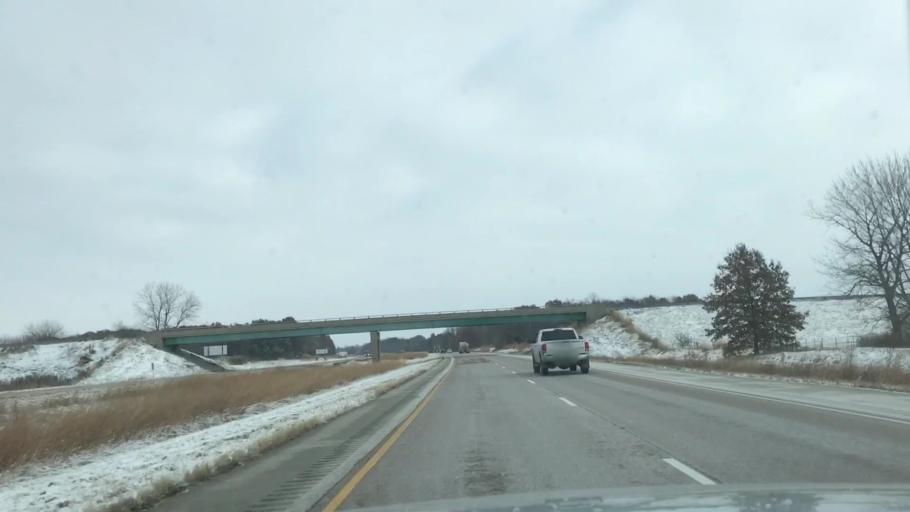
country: US
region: Illinois
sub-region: Macoupin County
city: Mount Olive
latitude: 39.0923
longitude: -89.7417
